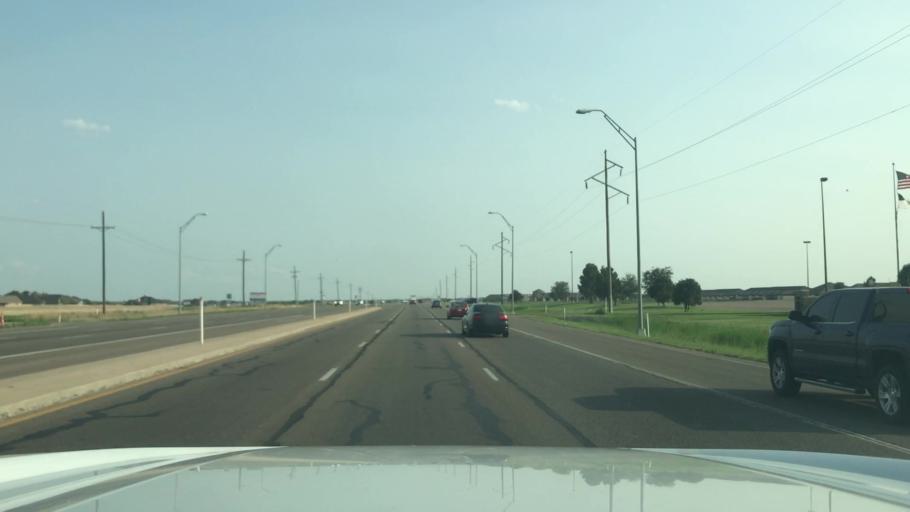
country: US
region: Texas
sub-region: Potter County
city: Amarillo
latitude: 35.1464
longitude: -101.9382
